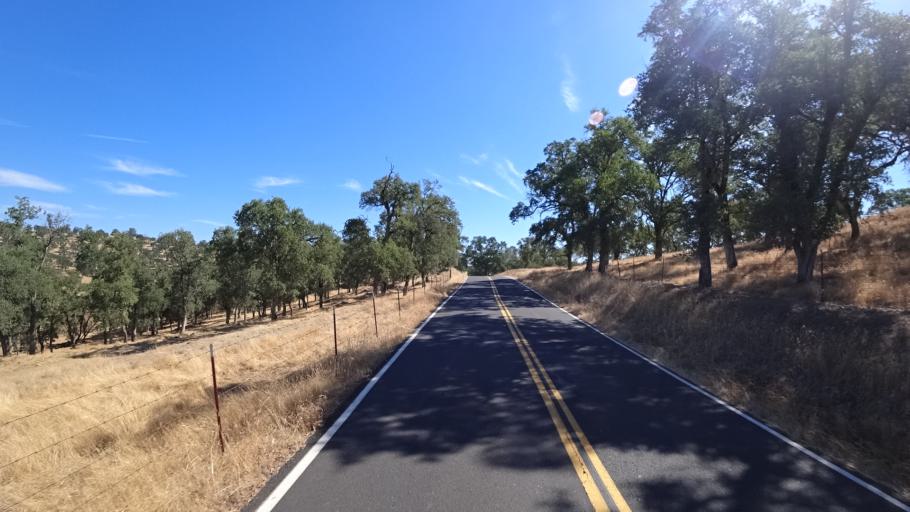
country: US
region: California
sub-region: Calaveras County
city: San Andreas
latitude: 38.1425
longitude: -120.6212
